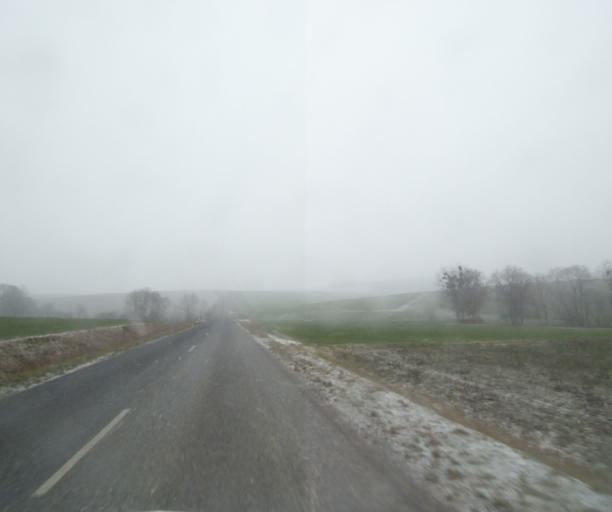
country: FR
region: Champagne-Ardenne
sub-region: Departement de la Haute-Marne
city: Wassy
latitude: 48.5071
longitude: 4.9846
